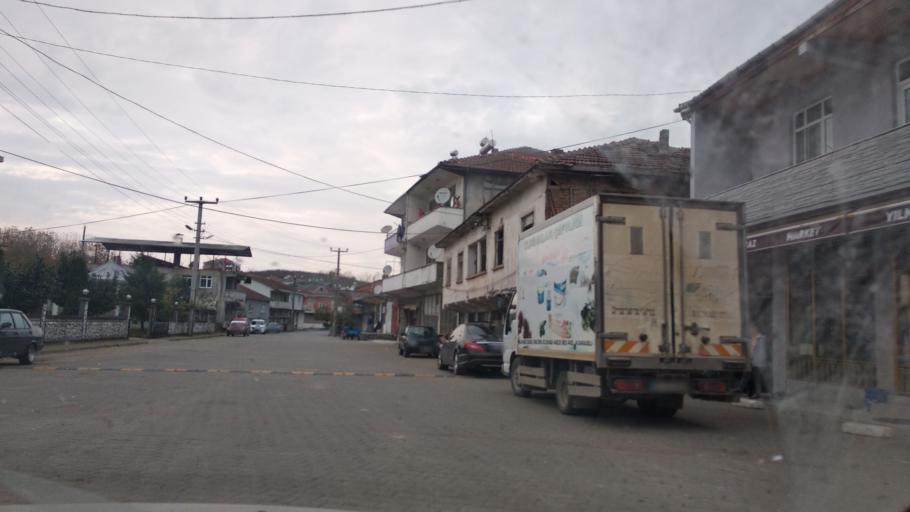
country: TR
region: Sakarya
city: Ortakoy
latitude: 41.0375
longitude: 30.6445
